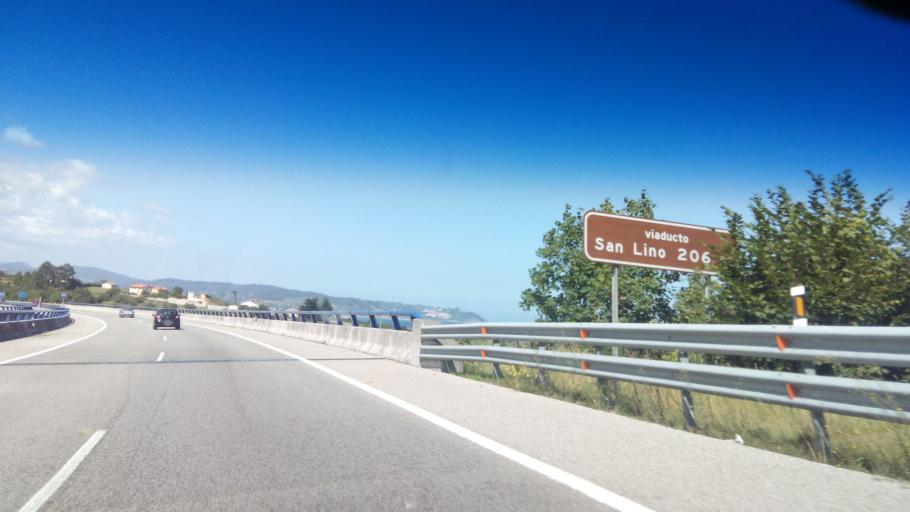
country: ES
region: Asturias
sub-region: Province of Asturias
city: Colunga
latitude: 43.4704
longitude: -5.1797
